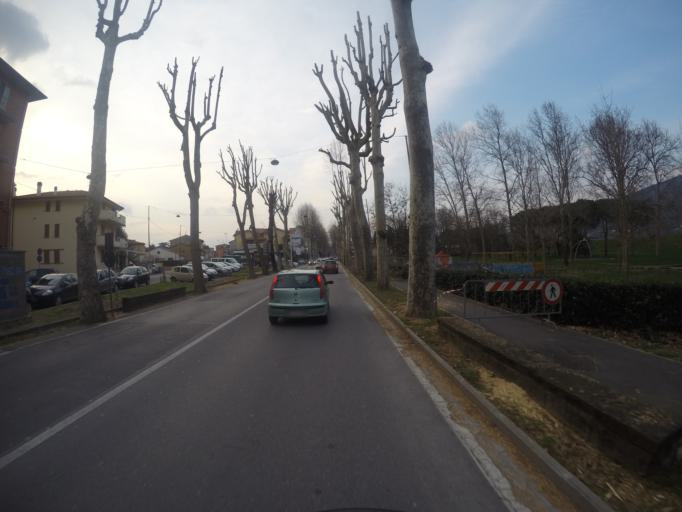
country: IT
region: Tuscany
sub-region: Provincia di Prato
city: Prato
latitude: 43.8631
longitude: 11.1183
